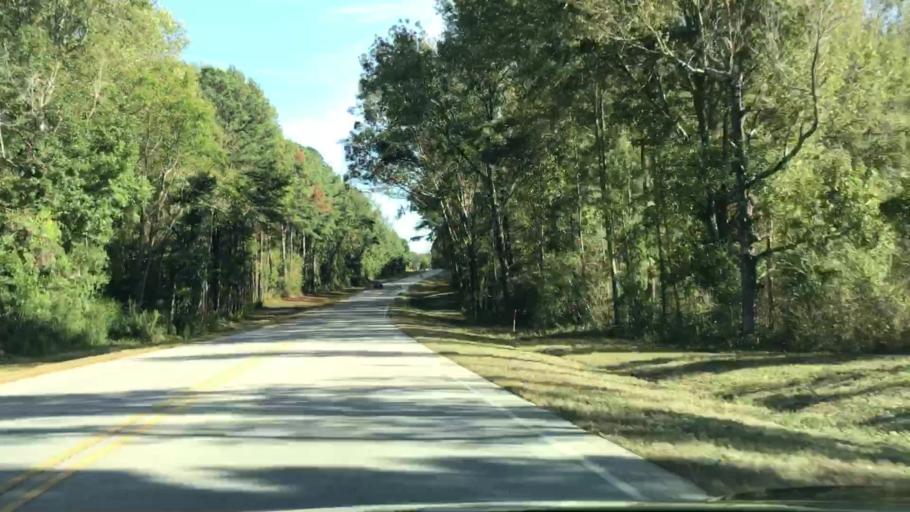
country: US
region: Georgia
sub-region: Warren County
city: Firing Range
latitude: 33.4672
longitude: -82.7145
